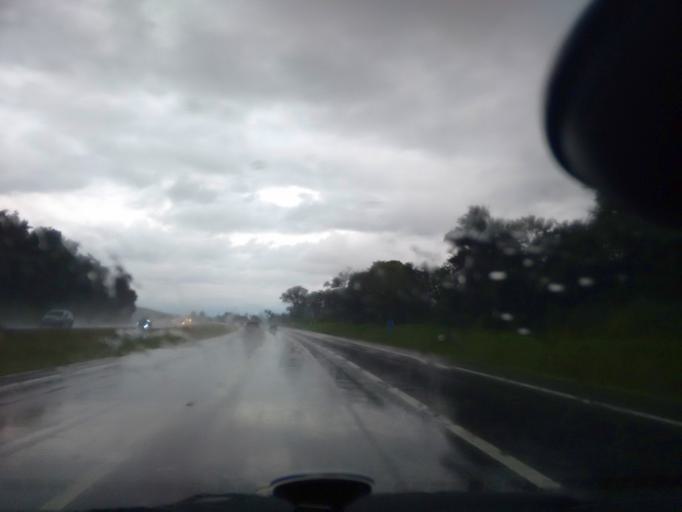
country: BR
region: Sao Paulo
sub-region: Limeira
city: Limeira
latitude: -22.5958
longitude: -47.4545
